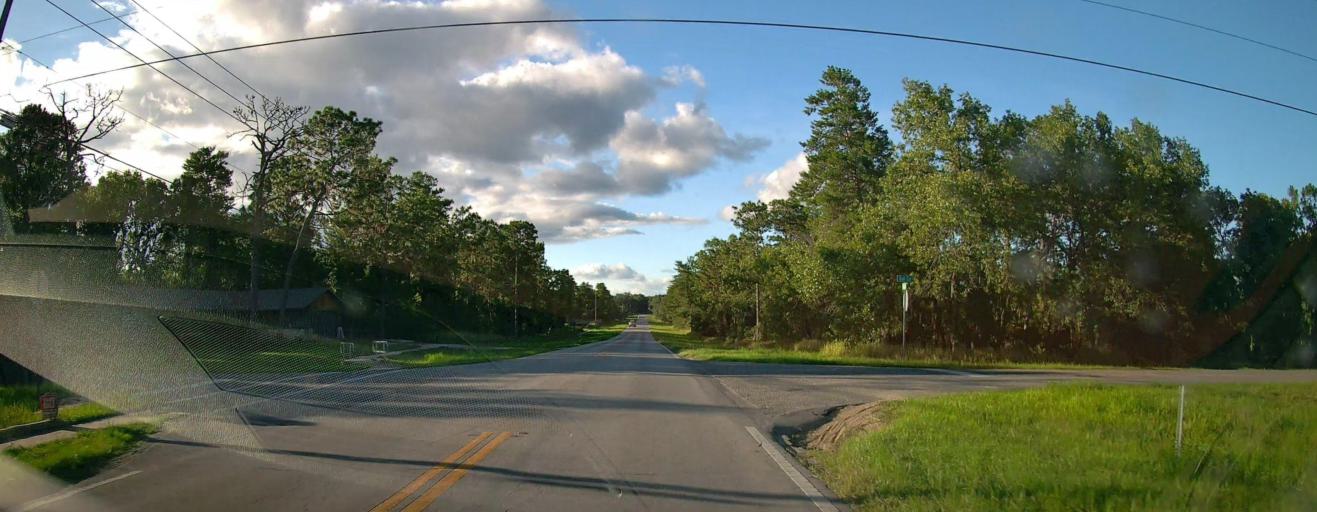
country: US
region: Florida
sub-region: Marion County
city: Silver Springs Shores
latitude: 29.0707
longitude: -82.0078
